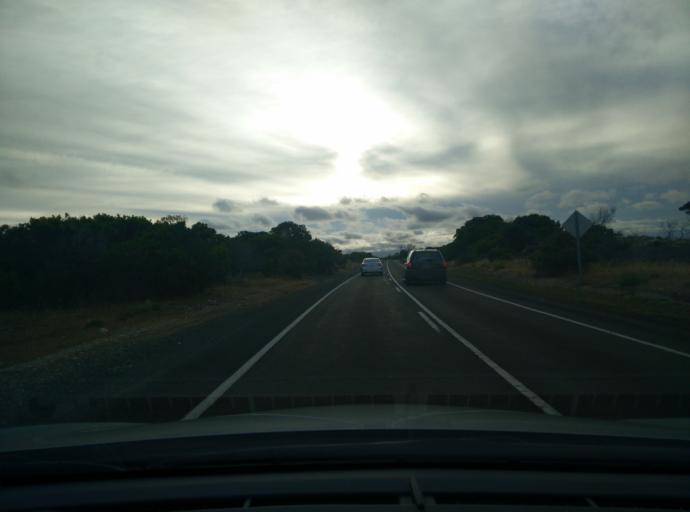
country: AU
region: South Australia
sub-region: Kangaroo Island
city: Kingscote
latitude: -35.8263
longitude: 137.8127
